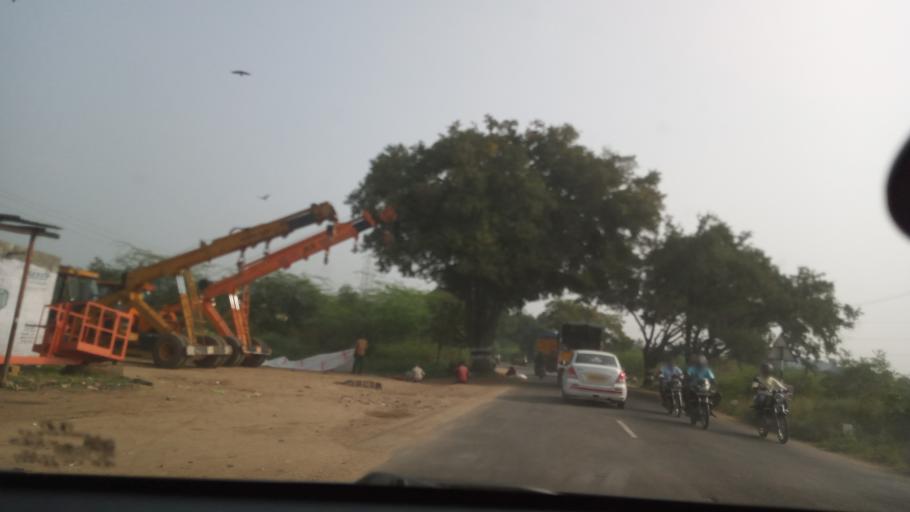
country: IN
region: Tamil Nadu
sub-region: Coimbatore
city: Annur
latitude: 11.1908
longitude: 77.0650
